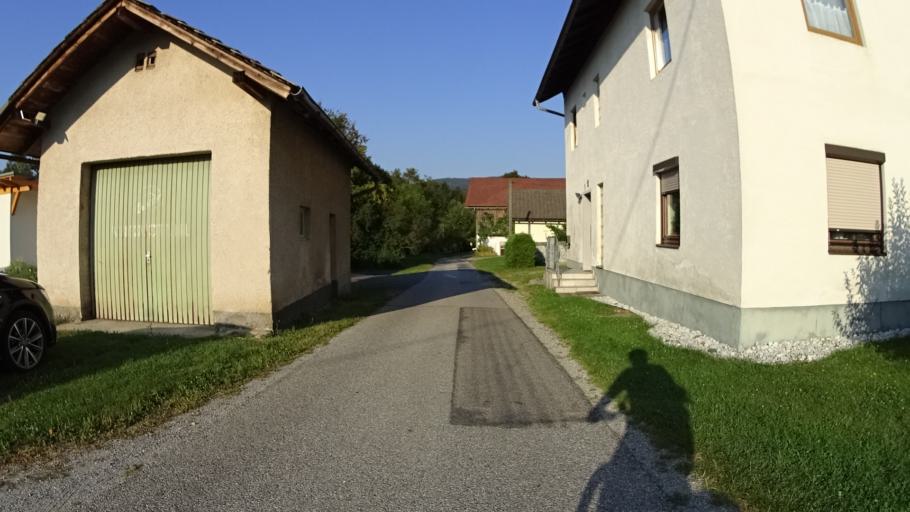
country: AT
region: Carinthia
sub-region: Politischer Bezirk Villach Land
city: Sankt Jakob
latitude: 46.5514
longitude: 14.0664
